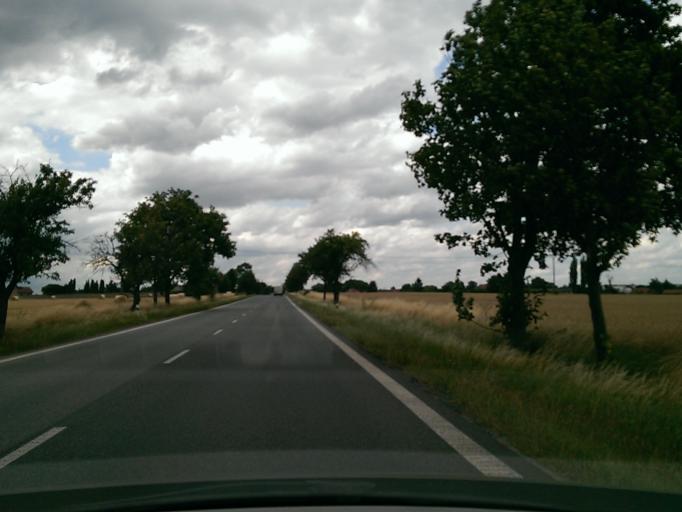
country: CZ
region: Central Bohemia
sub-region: Okres Nymburk
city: Nymburk
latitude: 50.2309
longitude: 15.0244
